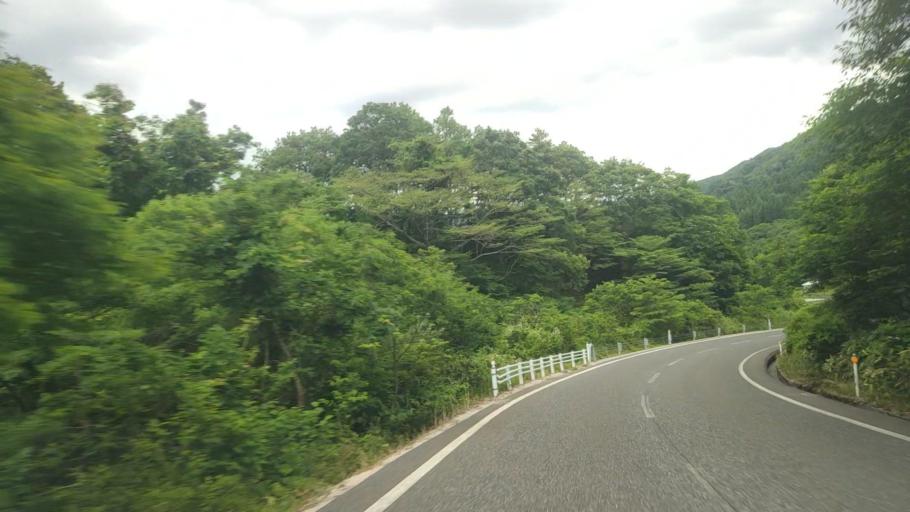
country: JP
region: Tottori
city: Kurayoshi
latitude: 35.2919
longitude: 133.9915
